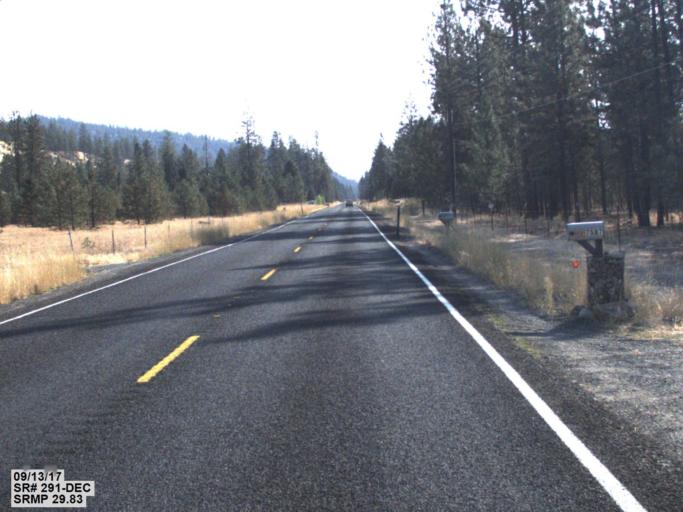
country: US
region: Washington
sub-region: Spokane County
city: Fairchild Air Force Base
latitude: 47.8393
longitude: -117.7918
